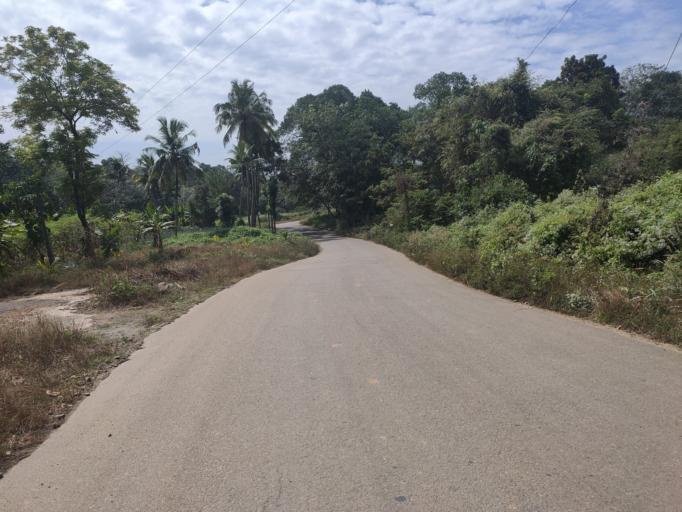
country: IN
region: Kerala
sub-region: Ernakulam
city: Kotamangalam
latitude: 10.0098
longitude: 76.6429
